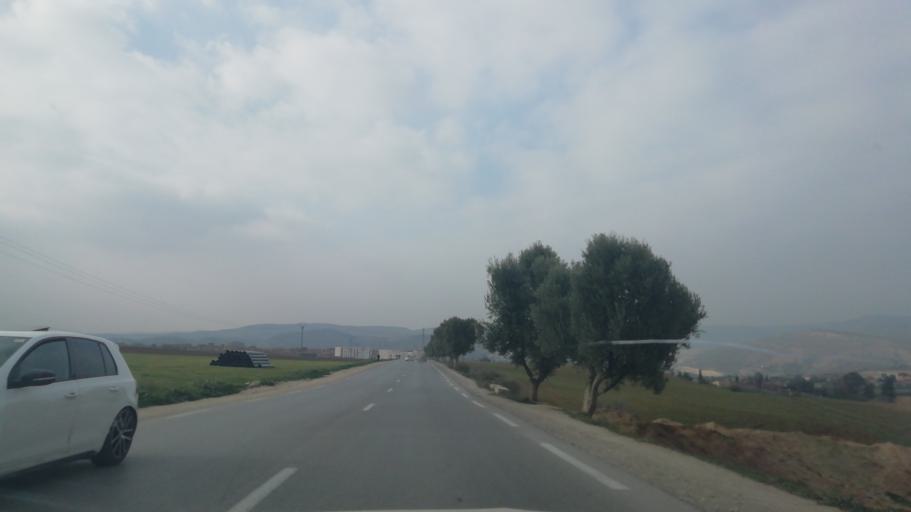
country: DZ
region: Mascara
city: Mascara
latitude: 35.4535
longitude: 0.0110
